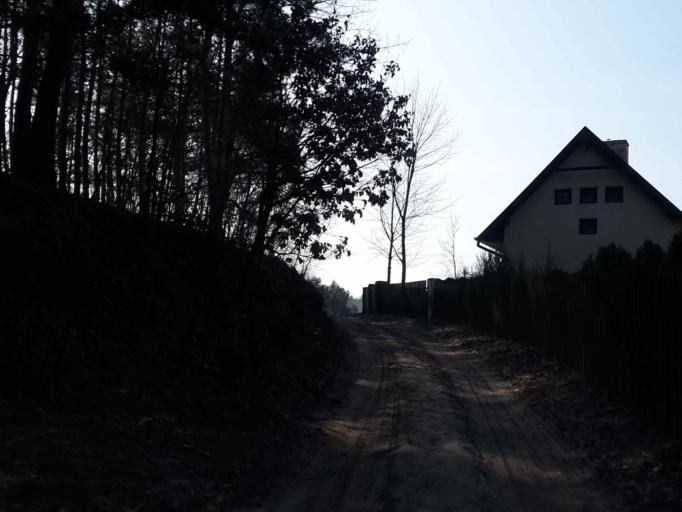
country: PL
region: Kujawsko-Pomorskie
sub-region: Powiat brodnicki
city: Brodnica
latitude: 53.3261
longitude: 19.3602
